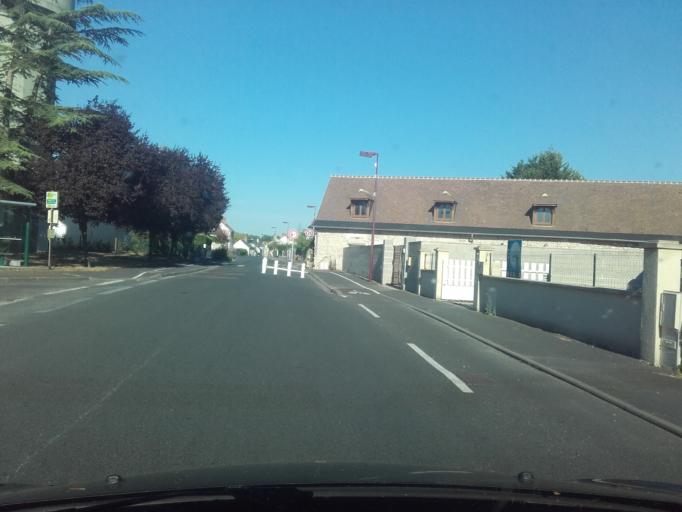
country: FR
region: Centre
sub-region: Departement d'Indre-et-Loire
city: Ambillou
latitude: 47.4507
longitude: 0.4525
